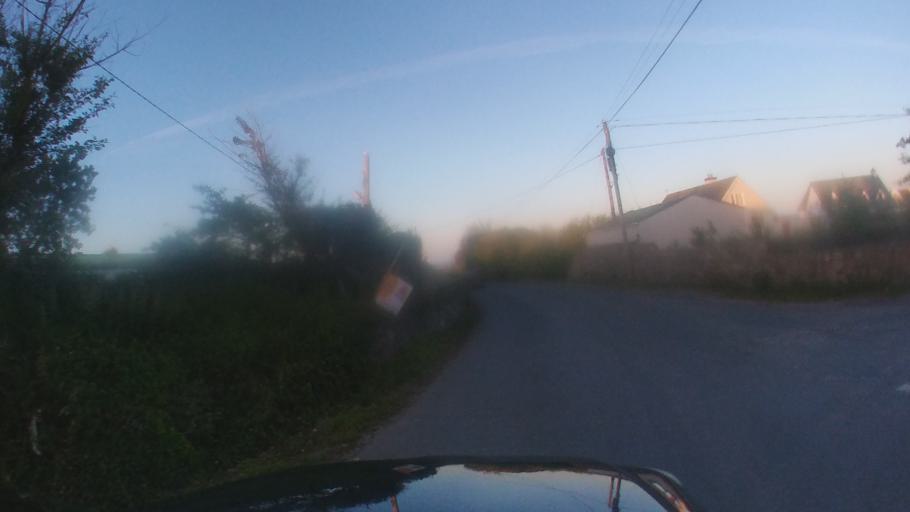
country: IE
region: Leinster
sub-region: Loch Garman
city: Ballygerry
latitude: 52.1978
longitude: -6.3575
